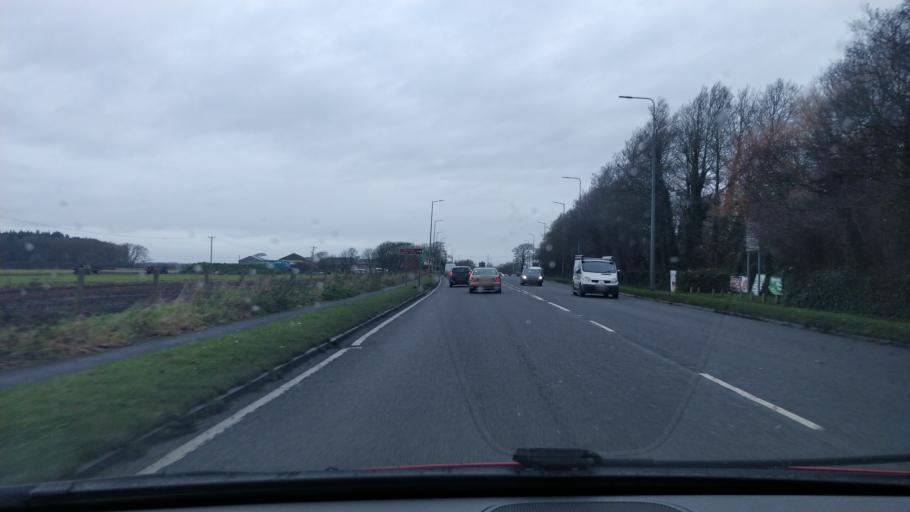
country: GB
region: England
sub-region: Sefton
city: Ince Blundell
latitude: 53.5237
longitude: -3.0298
